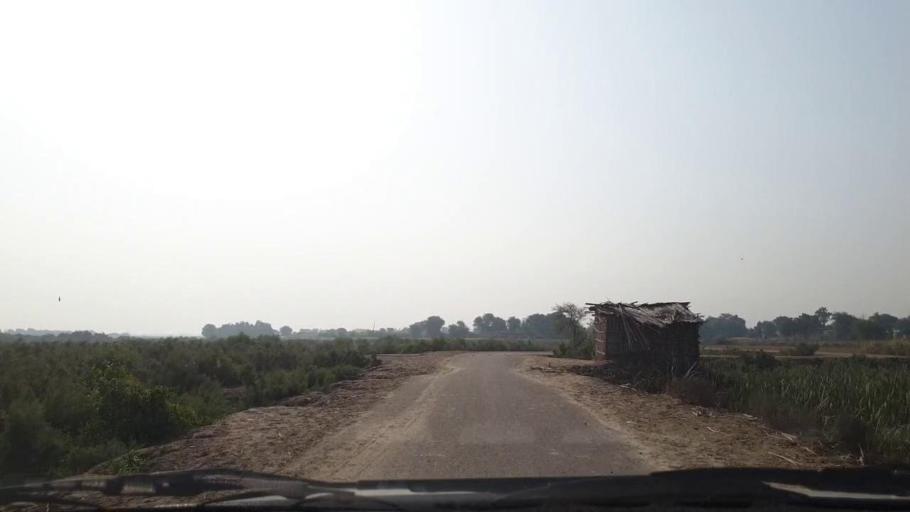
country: PK
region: Sindh
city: Tando Muhammad Khan
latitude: 25.0081
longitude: 68.4507
